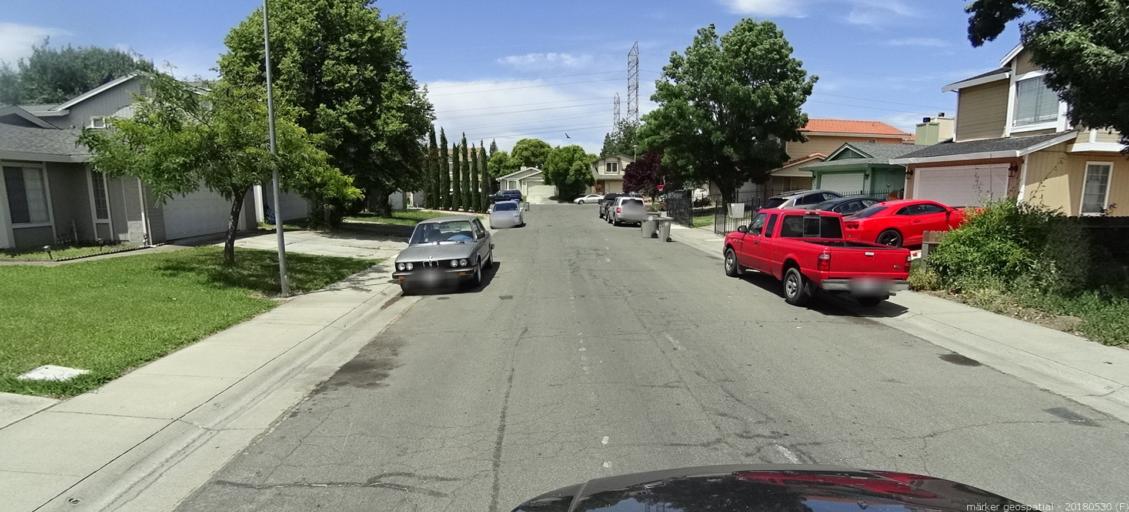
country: US
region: California
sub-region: Sacramento County
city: Sacramento
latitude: 38.6317
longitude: -121.4826
